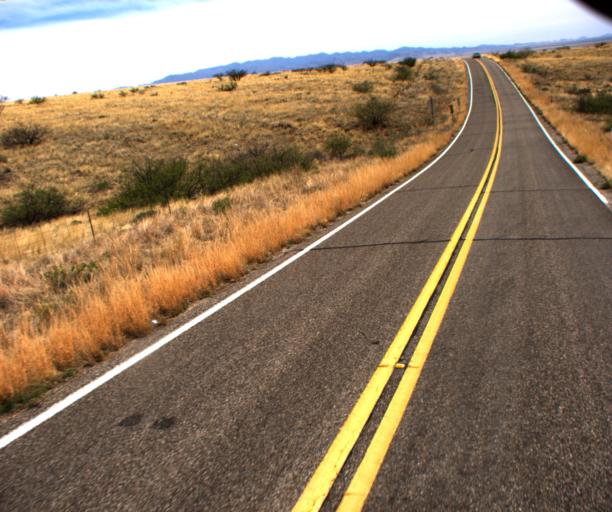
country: US
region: Arizona
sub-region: Cochise County
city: Willcox
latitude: 32.1419
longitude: -109.5652
